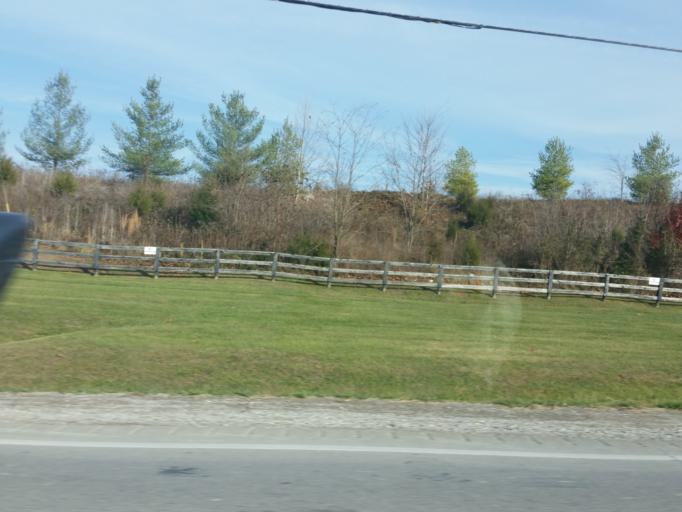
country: US
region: Kentucky
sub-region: Pendleton County
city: Falmouth
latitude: 38.7964
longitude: -84.3546
